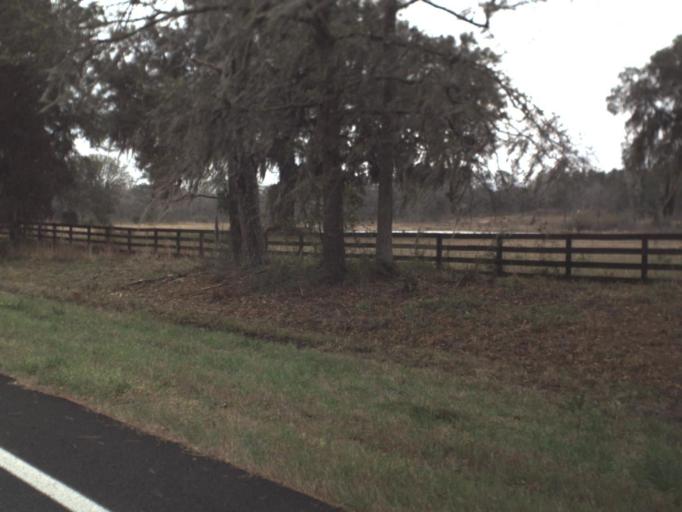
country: US
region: Florida
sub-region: Jefferson County
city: Monticello
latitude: 30.3874
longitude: -83.8437
